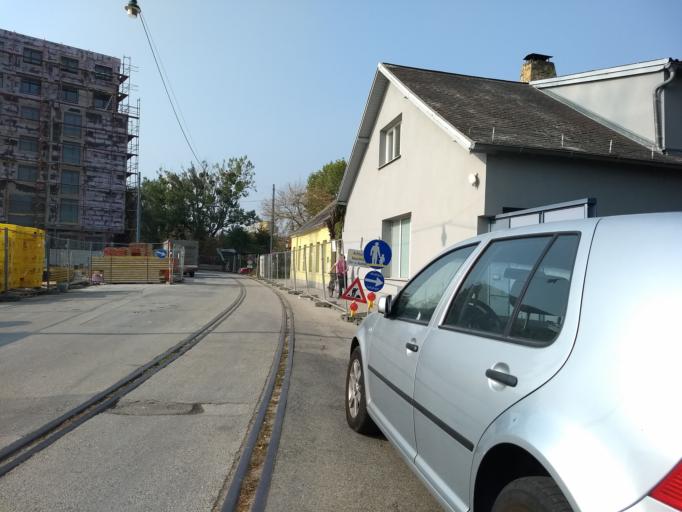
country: AT
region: Lower Austria
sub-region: Politischer Bezirk Modling
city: Perchtoldsdorf
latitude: 48.1346
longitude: 16.2876
